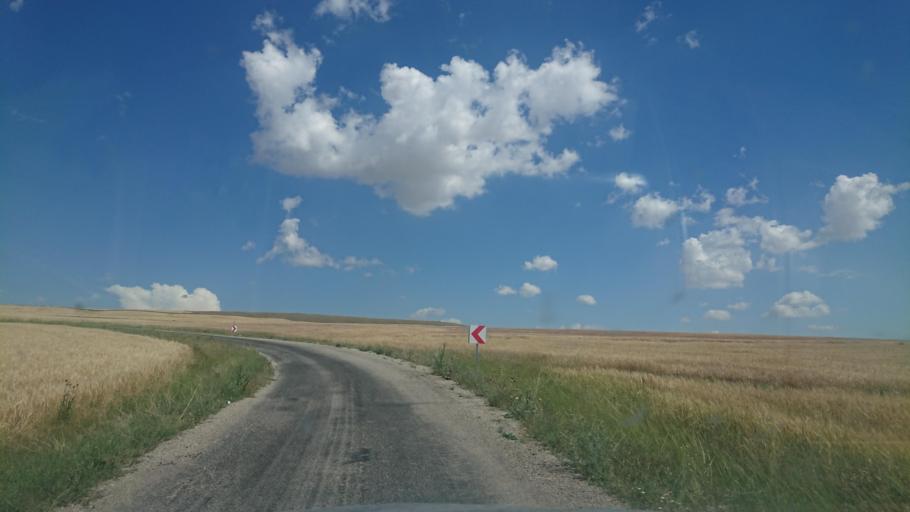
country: TR
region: Aksaray
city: Agacoren
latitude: 38.8066
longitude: 33.8016
